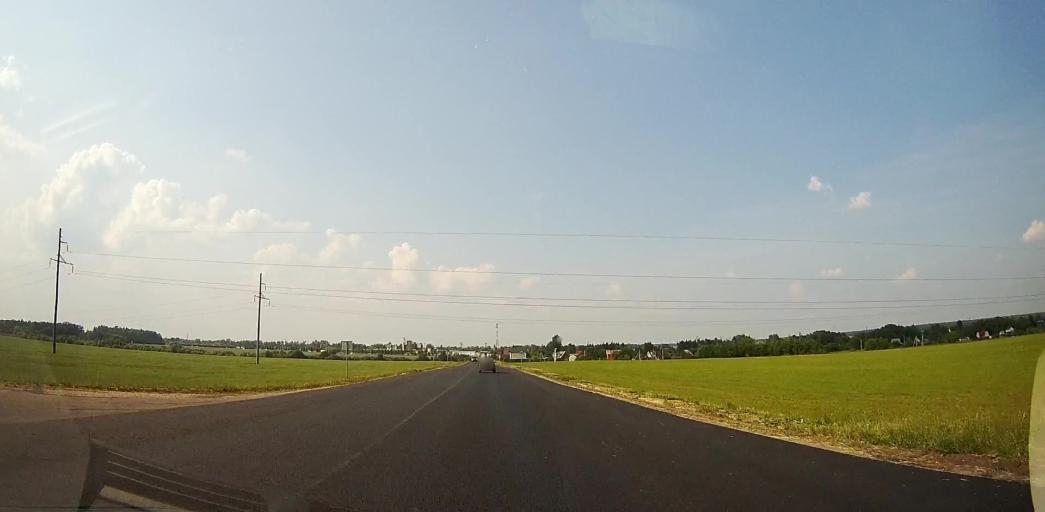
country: RU
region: Moskovskaya
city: Barybino
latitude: 55.2446
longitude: 37.9161
